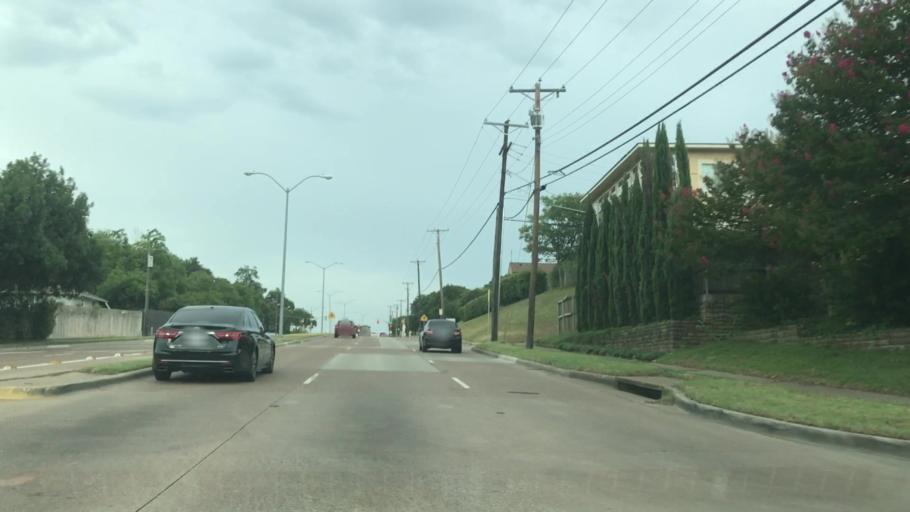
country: US
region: Texas
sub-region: Dallas County
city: Richardson
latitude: 32.8789
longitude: -96.7114
